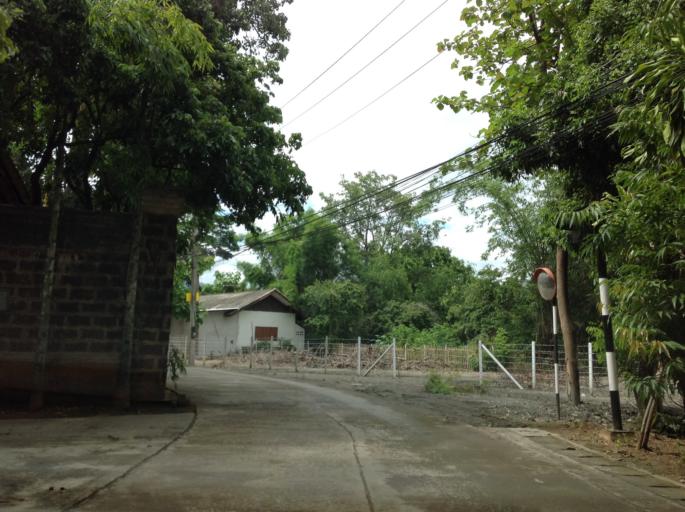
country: TH
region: Chiang Mai
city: Hang Dong
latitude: 18.7080
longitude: 98.9220
